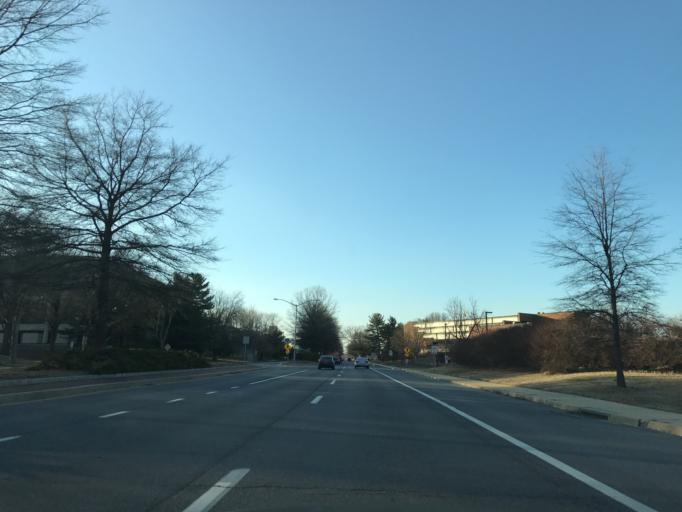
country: US
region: Maryland
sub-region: Anne Arundel County
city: Annapolis
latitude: 38.9851
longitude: -76.4995
